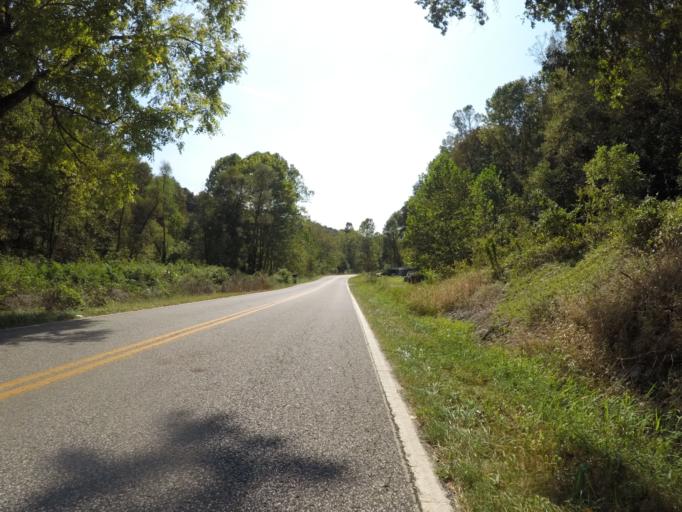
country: US
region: West Virginia
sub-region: Cabell County
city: Lesage
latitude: 38.5617
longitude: -82.3945
